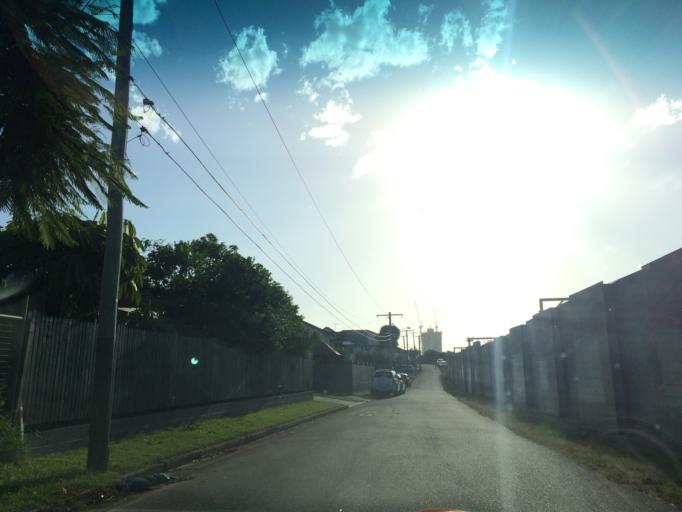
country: AU
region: Queensland
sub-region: Brisbane
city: Greenslopes
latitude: -27.4929
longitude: 153.0518
